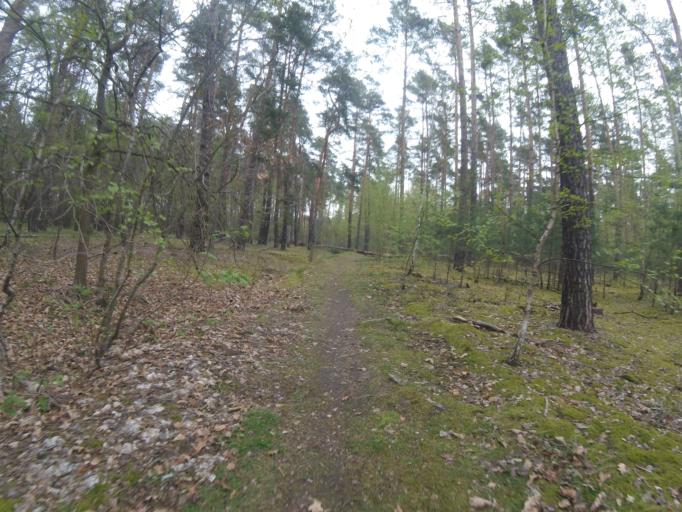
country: DE
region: Brandenburg
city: Bestensee
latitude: 52.2468
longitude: 13.6652
